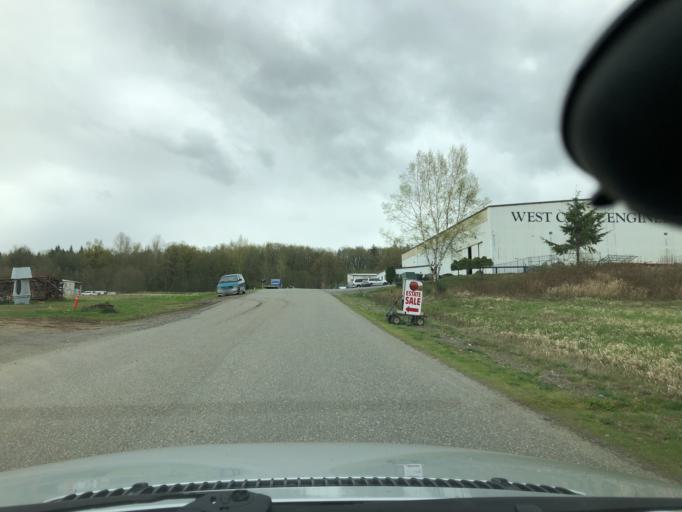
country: US
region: Washington
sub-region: Whatcom County
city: Ferndale
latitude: 48.8913
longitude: -122.6042
